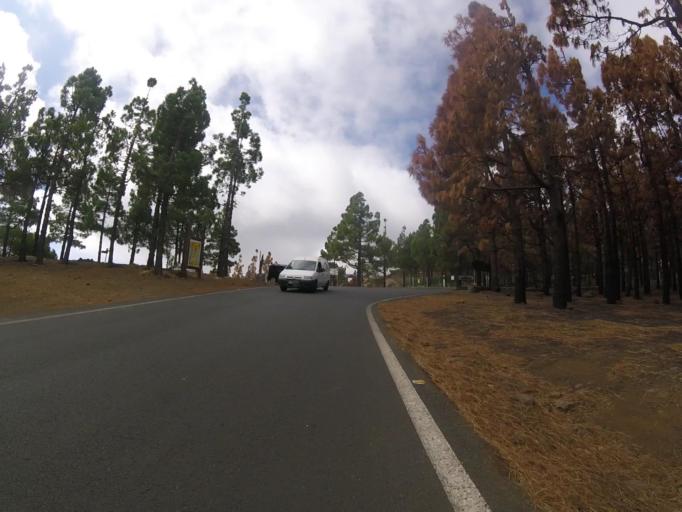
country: ES
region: Canary Islands
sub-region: Provincia de Las Palmas
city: San Bartolome
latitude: 27.9635
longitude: -15.5691
